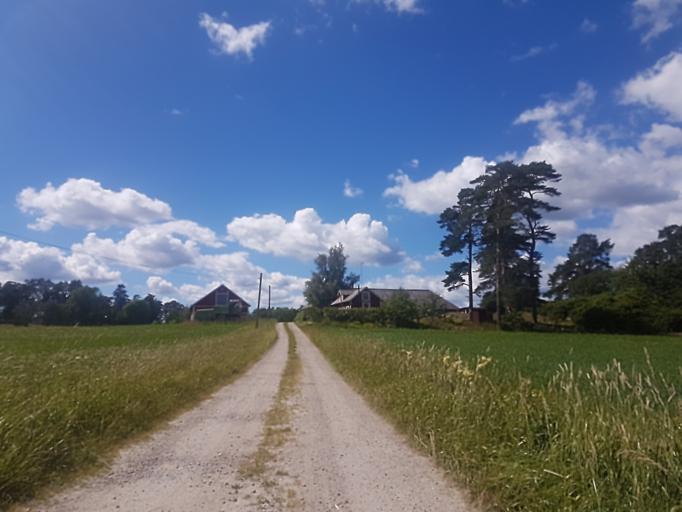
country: SE
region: Stockholm
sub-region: Sodertalje Kommun
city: Molnbo
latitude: 59.0019
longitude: 17.3765
